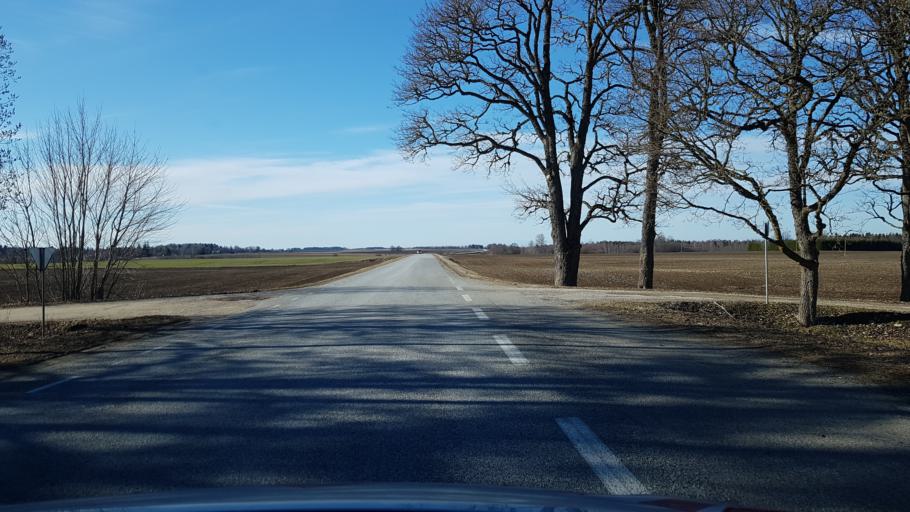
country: EE
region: Laeaene-Virumaa
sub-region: Kadrina vald
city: Kadrina
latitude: 59.3108
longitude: 26.1570
